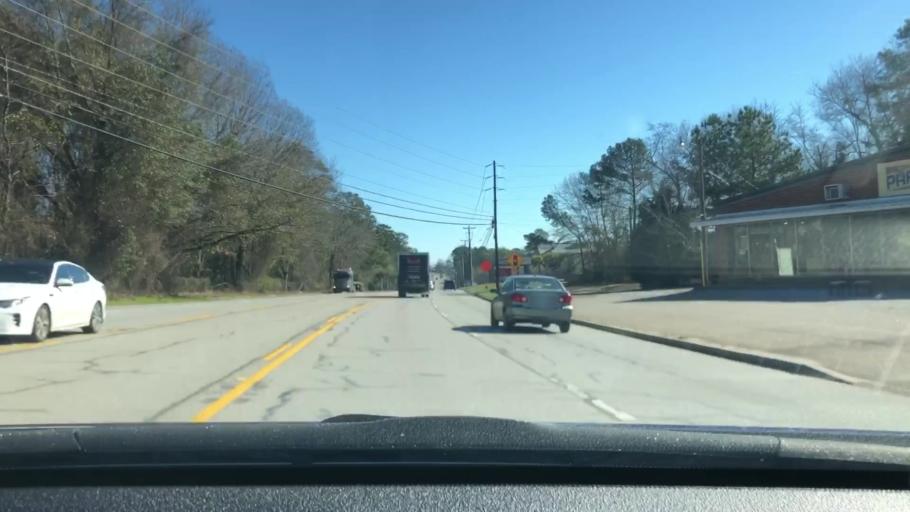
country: US
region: South Carolina
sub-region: Lexington County
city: Oak Grove
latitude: 34.0076
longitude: -81.1261
